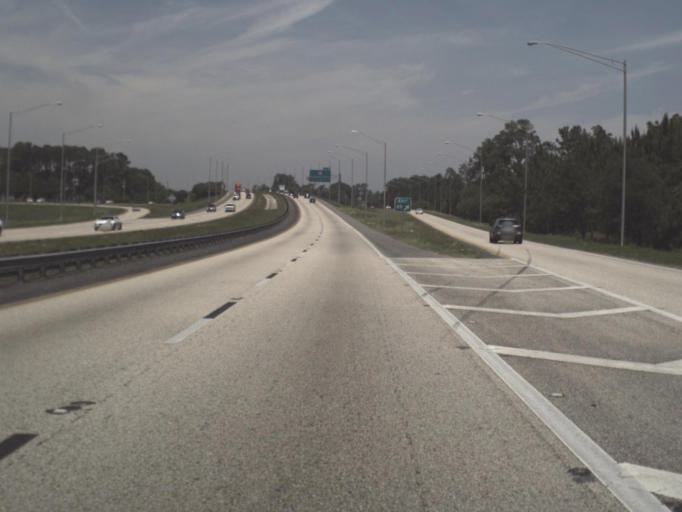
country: US
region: Florida
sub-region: Duval County
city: Atlantic Beach
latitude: 30.3111
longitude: -81.5237
